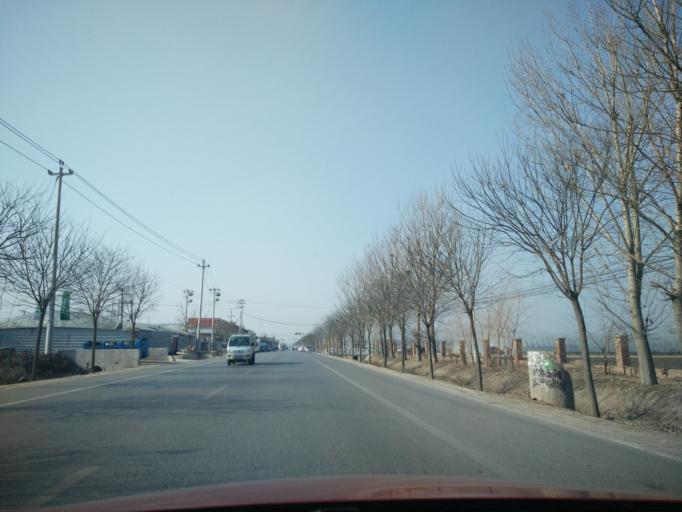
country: CN
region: Beijing
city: Yinghai
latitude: 39.7056
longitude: 116.4375
